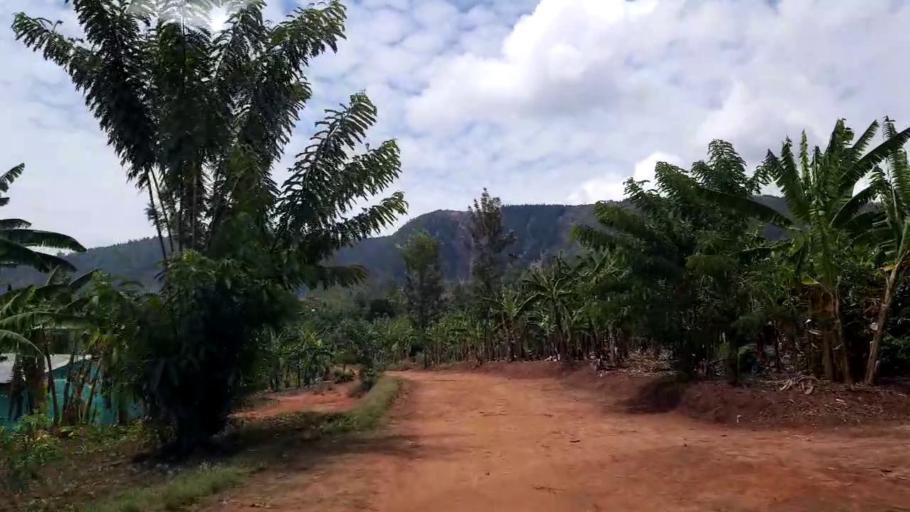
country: RW
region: Northern Province
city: Byumba
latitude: -1.4921
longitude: 30.1967
